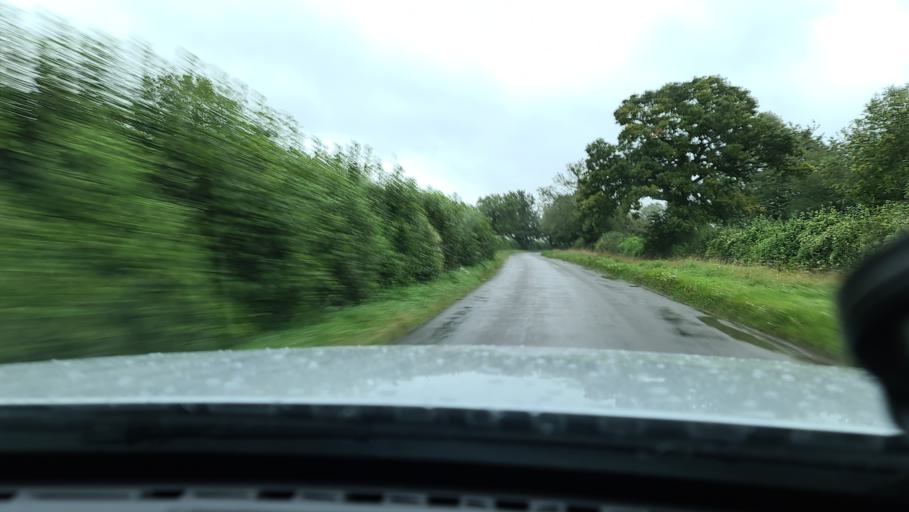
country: GB
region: England
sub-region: Oxfordshire
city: Woodstock
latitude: 51.9113
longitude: -1.3799
